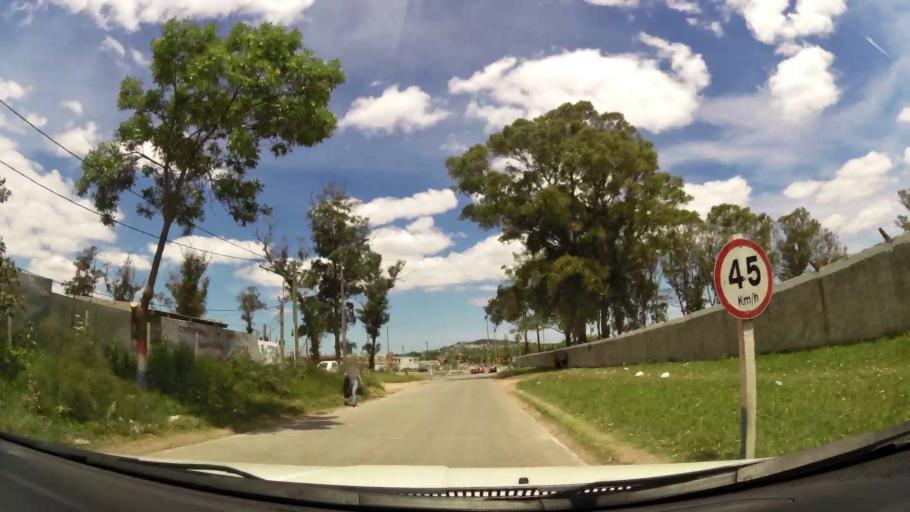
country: UY
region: Montevideo
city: Montevideo
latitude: -34.8630
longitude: -56.2521
